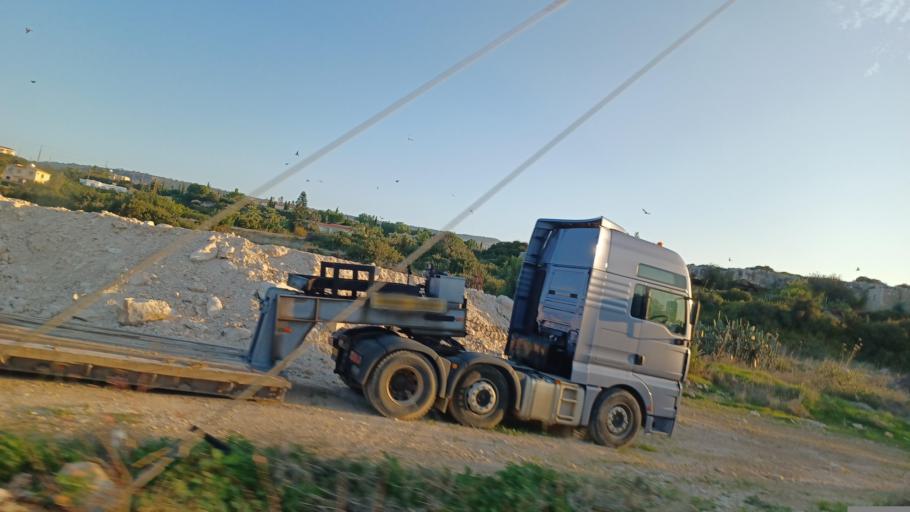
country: CY
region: Pafos
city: Pegeia
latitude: 34.8684
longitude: 32.3538
